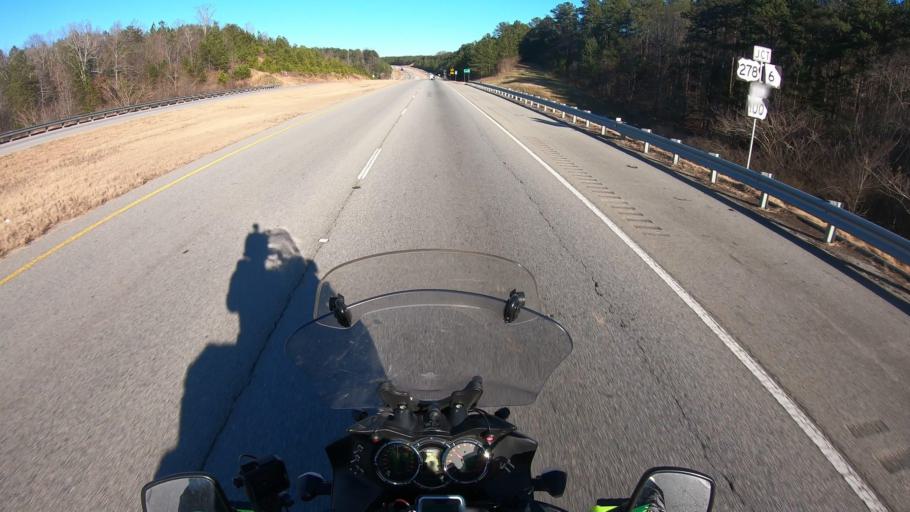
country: US
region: Georgia
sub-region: Polk County
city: Cedartown
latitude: 33.9924
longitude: -85.2397
